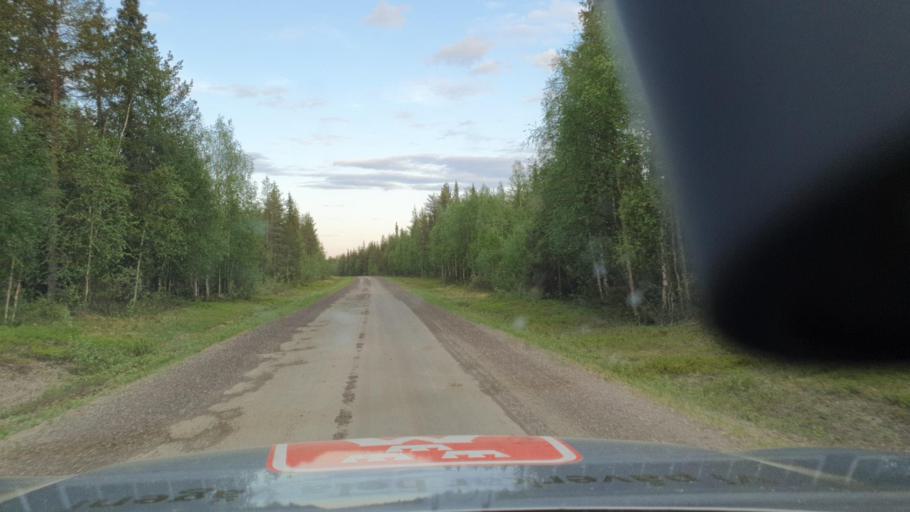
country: SE
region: Norrbotten
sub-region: Bodens Kommun
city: Boden
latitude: 66.5842
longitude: 21.3964
